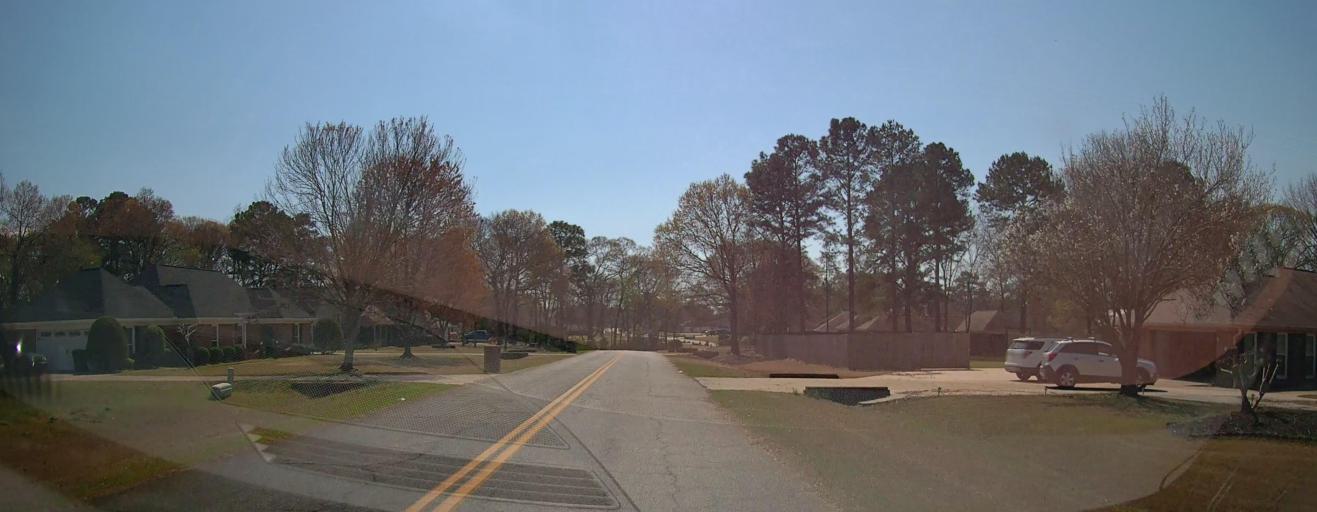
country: US
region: Georgia
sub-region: Houston County
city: Centerville
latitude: 32.6089
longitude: -83.6908
